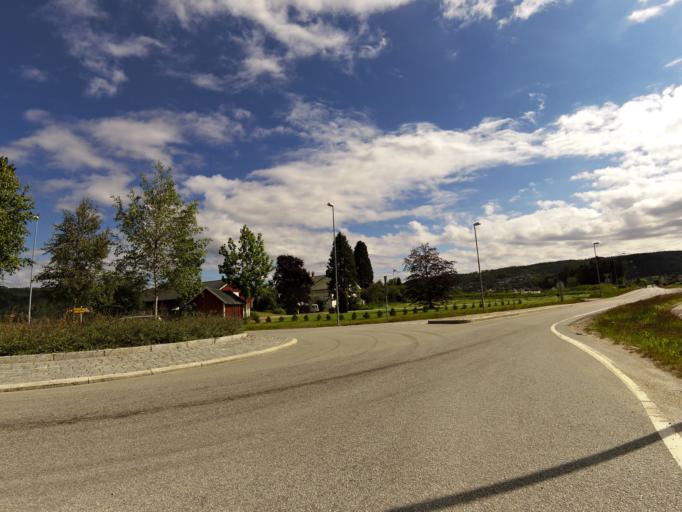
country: NO
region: Vest-Agder
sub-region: Vennesla
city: Vennesla
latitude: 58.2683
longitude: 7.9543
